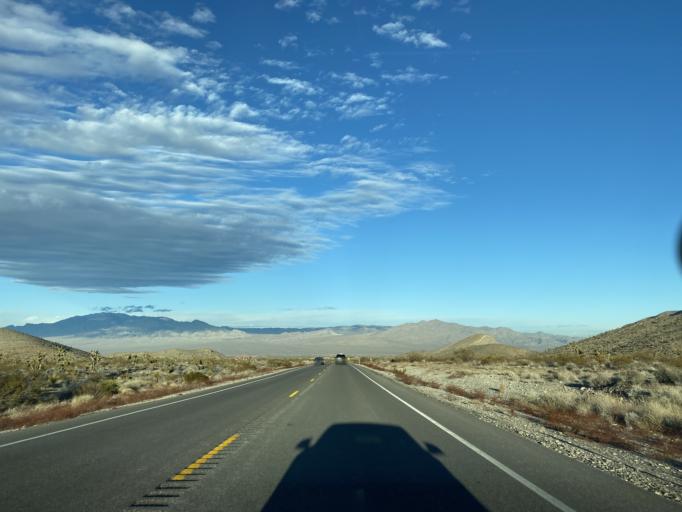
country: US
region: Nevada
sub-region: Clark County
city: Summerlin South
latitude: 36.2894
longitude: -115.4298
